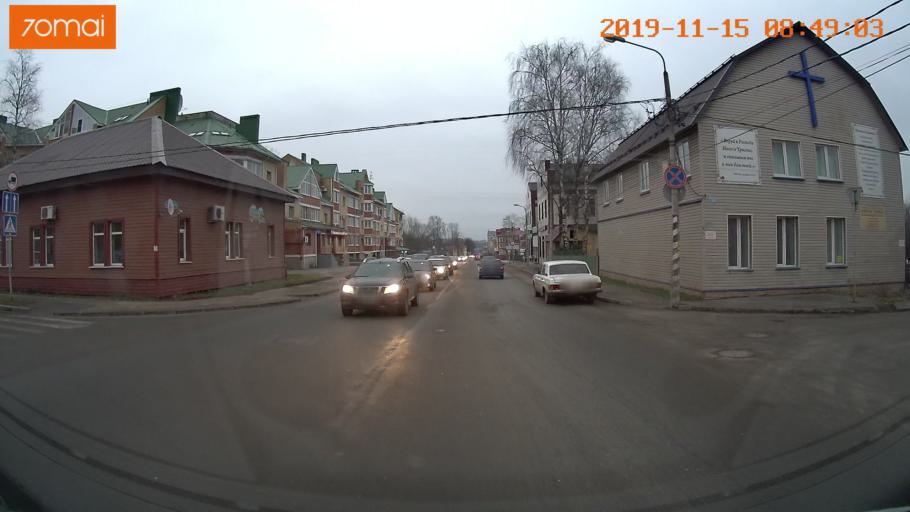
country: RU
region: Vologda
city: Cherepovets
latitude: 59.1221
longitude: 37.9210
